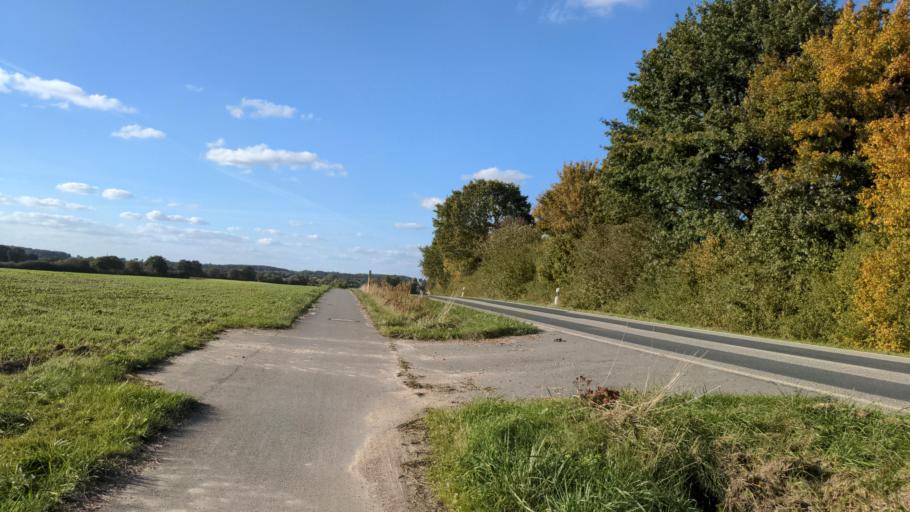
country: DE
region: Schleswig-Holstein
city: Zarpen
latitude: 53.8610
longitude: 10.5363
